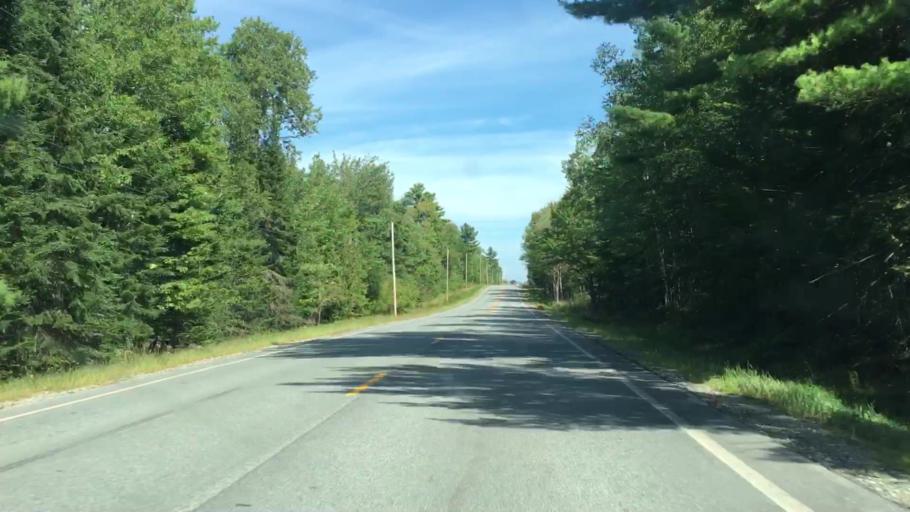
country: US
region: Maine
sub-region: Penobscot County
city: Howland
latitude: 45.2333
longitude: -68.6912
